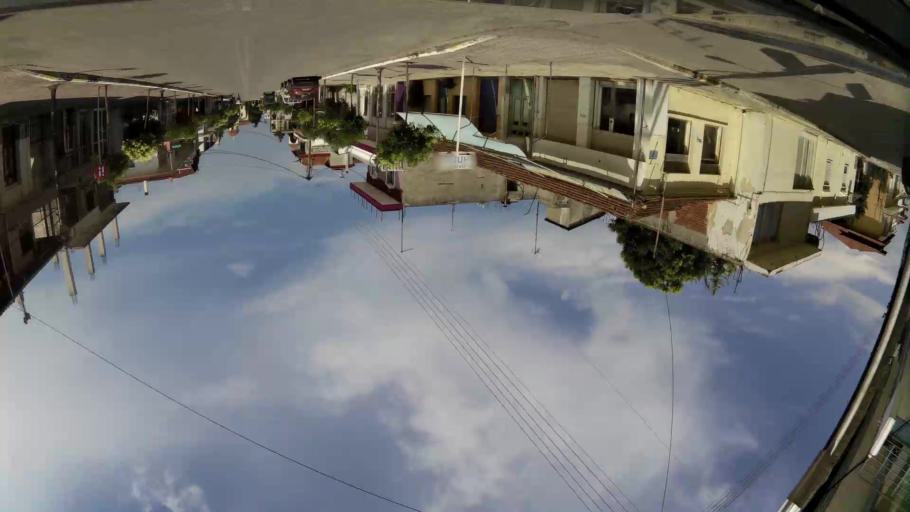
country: GR
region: Central Macedonia
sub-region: Nomos Pierias
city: Korinos
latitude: 40.3155
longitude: 22.5834
